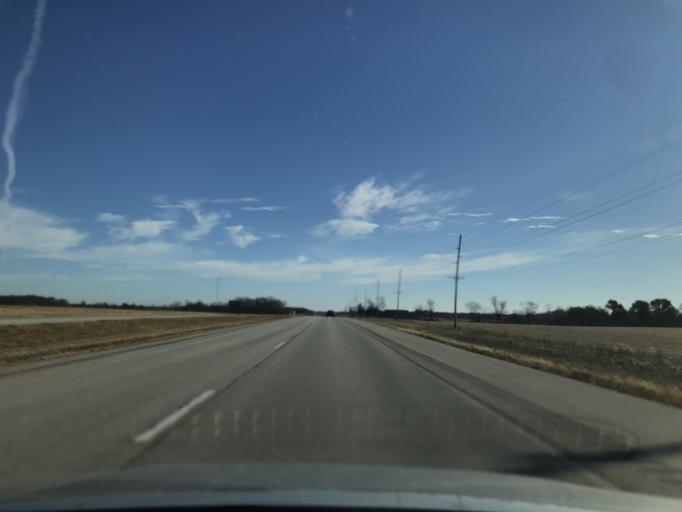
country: US
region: Illinois
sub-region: Hancock County
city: Carthage
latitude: 40.4149
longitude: -91.0489
